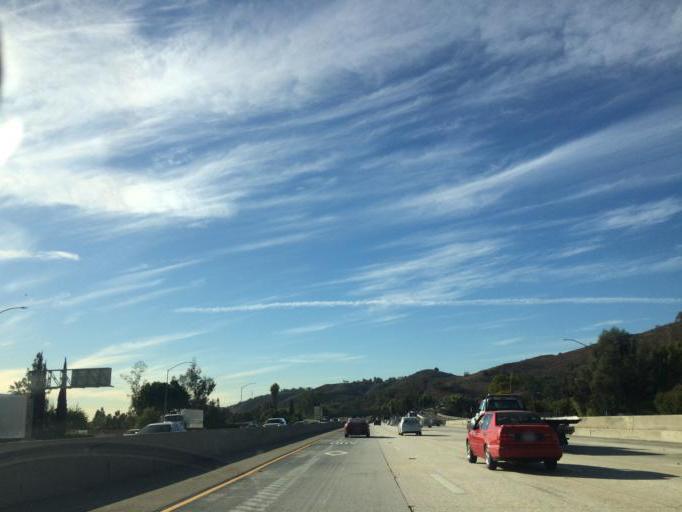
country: US
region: California
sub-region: Los Angeles County
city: La Verne
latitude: 34.0729
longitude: -117.7817
